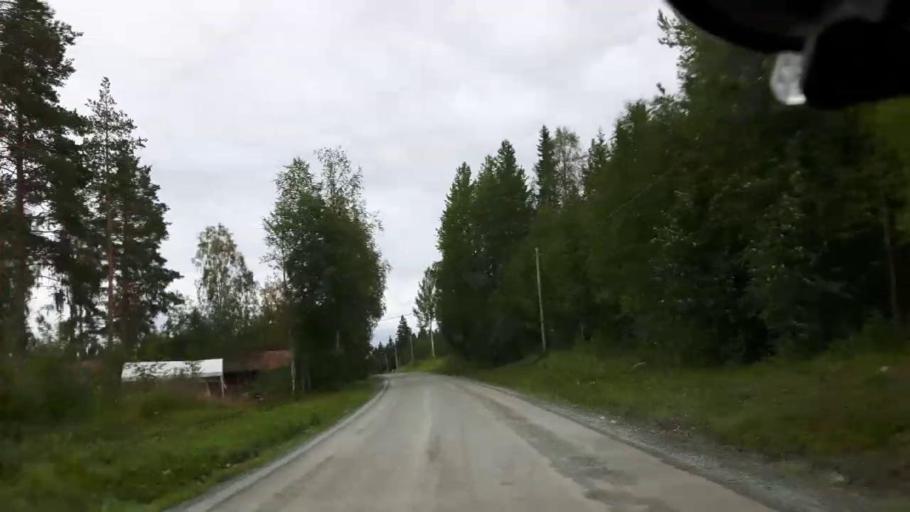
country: SE
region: Jaemtland
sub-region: Braecke Kommun
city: Braecke
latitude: 63.0708
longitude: 15.3028
